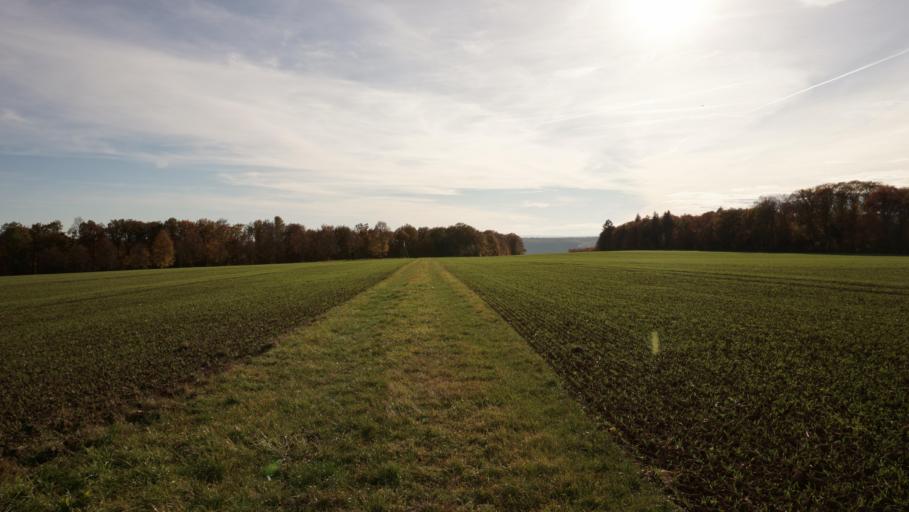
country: DE
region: Baden-Wuerttemberg
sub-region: Karlsruhe Region
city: Hassmersheim
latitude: 49.3164
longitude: 9.1605
